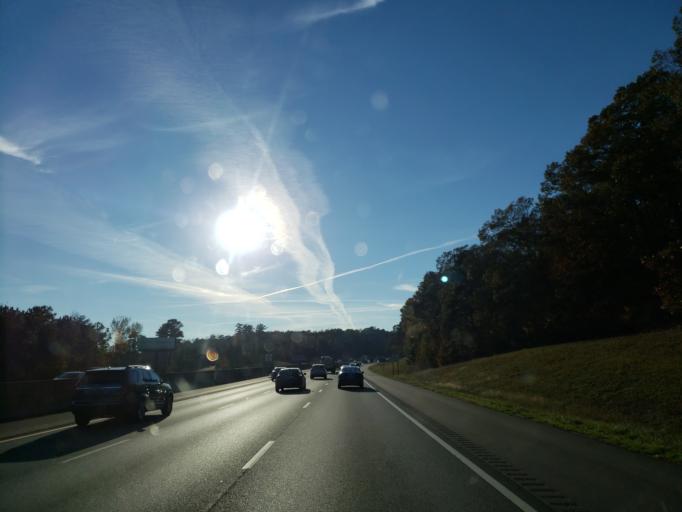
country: US
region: Alabama
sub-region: Tuscaloosa County
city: Coaling
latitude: 33.1795
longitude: -87.3742
